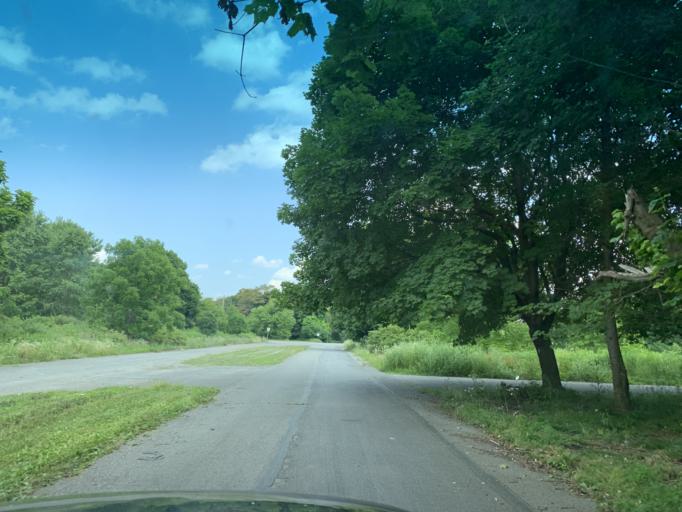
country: US
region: Pennsylvania
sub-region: Schuylkill County
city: Ashland
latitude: 40.8051
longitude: -76.3427
